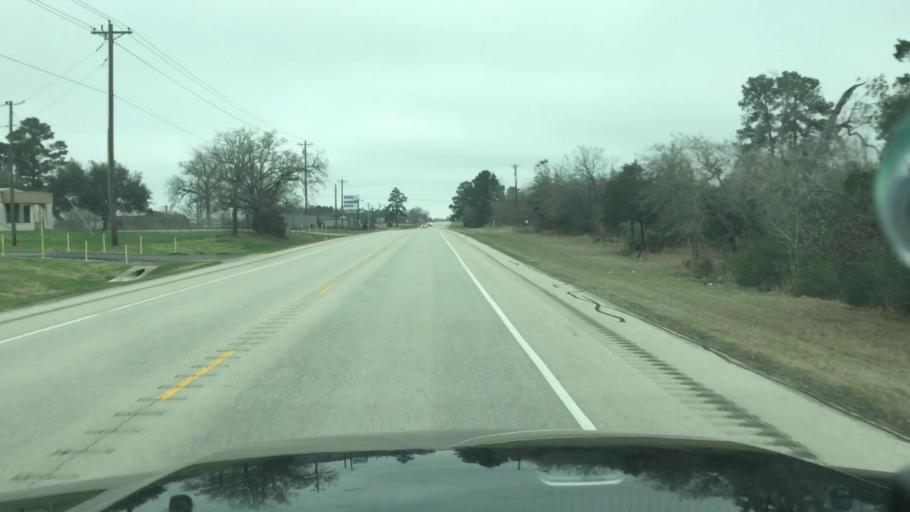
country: US
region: Texas
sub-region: Lee County
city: Giddings
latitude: 30.0486
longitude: -96.9142
